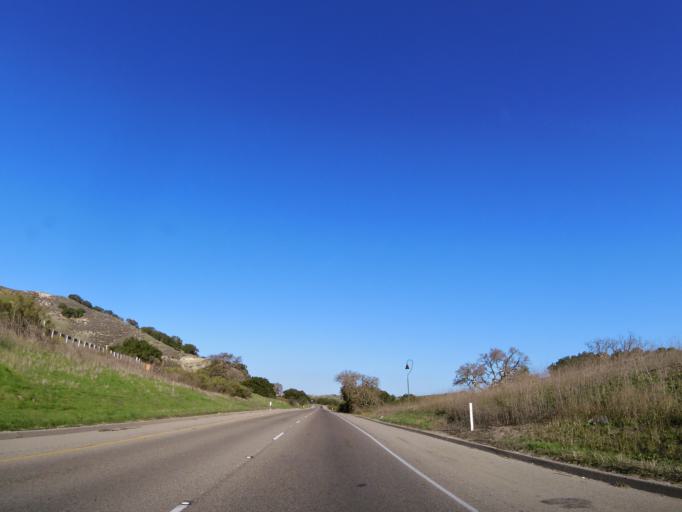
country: US
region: California
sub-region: Santa Barbara County
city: Los Olivos
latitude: 34.6934
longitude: -120.1600
